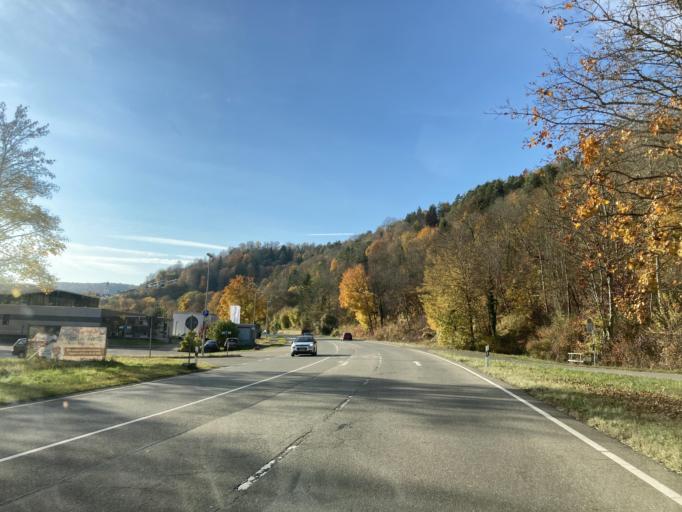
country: DE
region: Baden-Wuerttemberg
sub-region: Karlsruhe Region
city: Horb am Neckar
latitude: 48.4485
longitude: 8.7030
